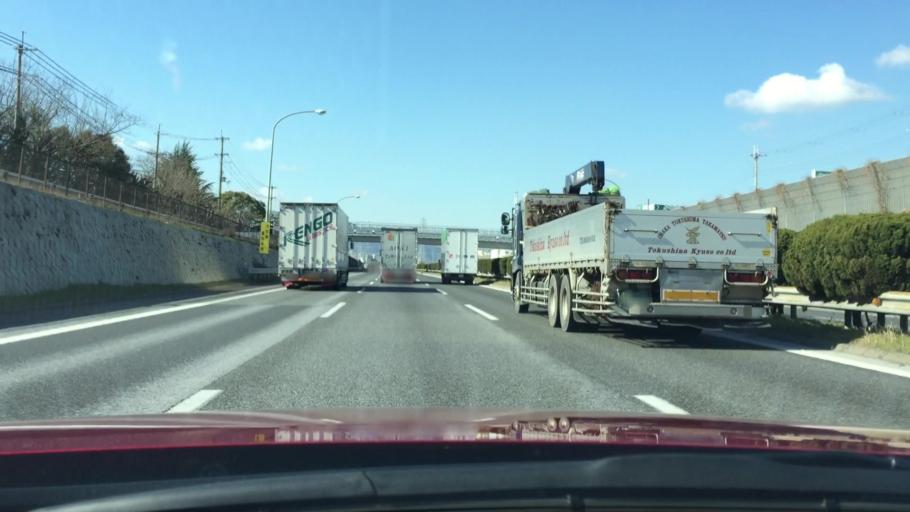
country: JP
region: Hyogo
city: Kawanishi
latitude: 34.8110
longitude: 135.4018
